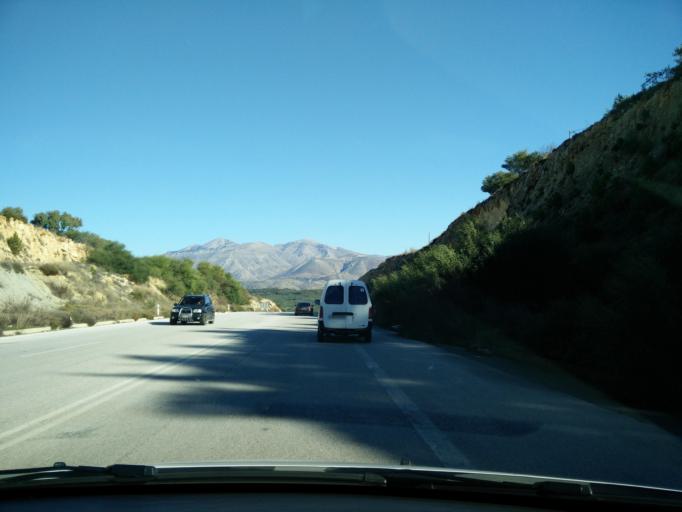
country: GR
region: Crete
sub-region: Nomos Irakleiou
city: Arkalochori
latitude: 35.1347
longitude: 25.2674
